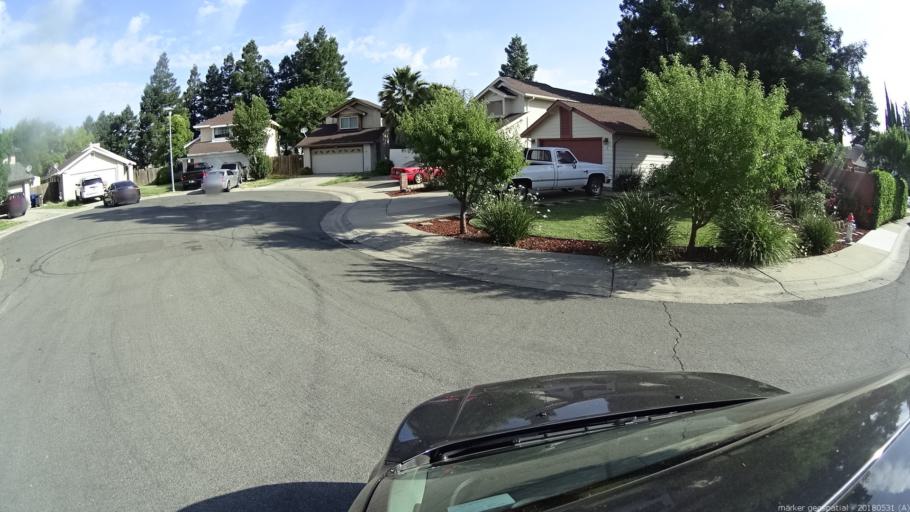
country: US
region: California
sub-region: Sacramento County
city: Sacramento
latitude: 38.6341
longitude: -121.4925
